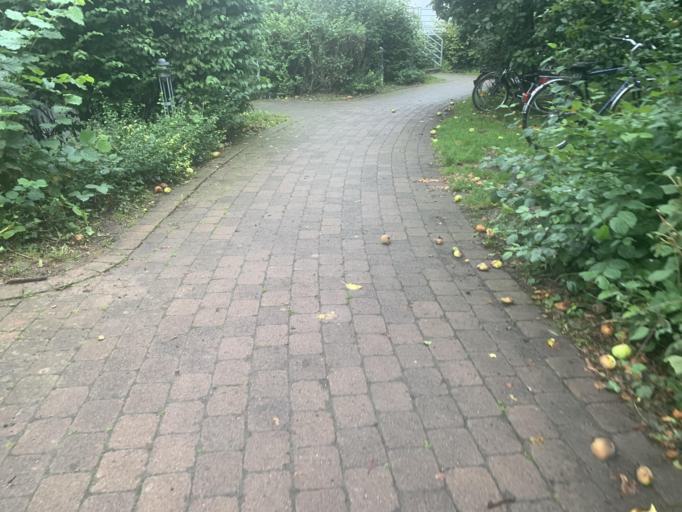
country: DE
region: Lower Saxony
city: Goettingen
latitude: 51.5604
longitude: 9.9507
